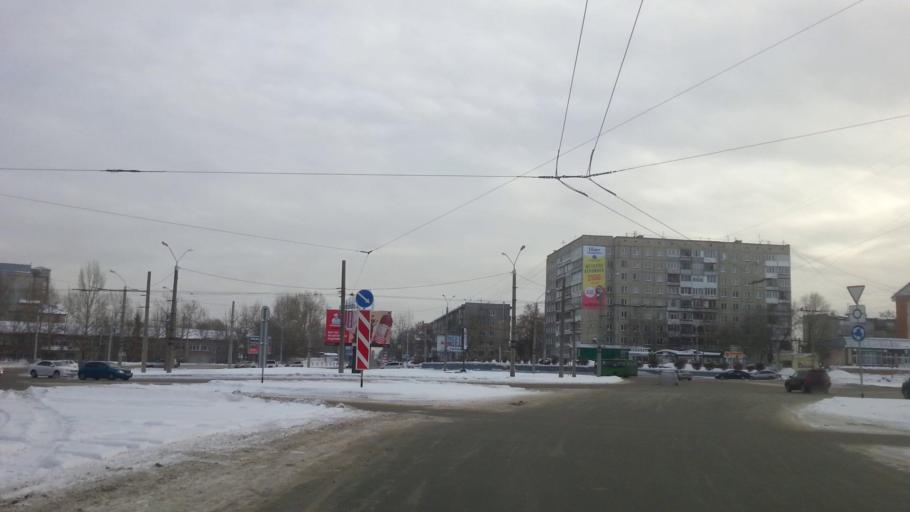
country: RU
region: Altai Krai
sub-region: Gorod Barnaulskiy
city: Barnaul
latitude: 53.3681
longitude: 83.7061
